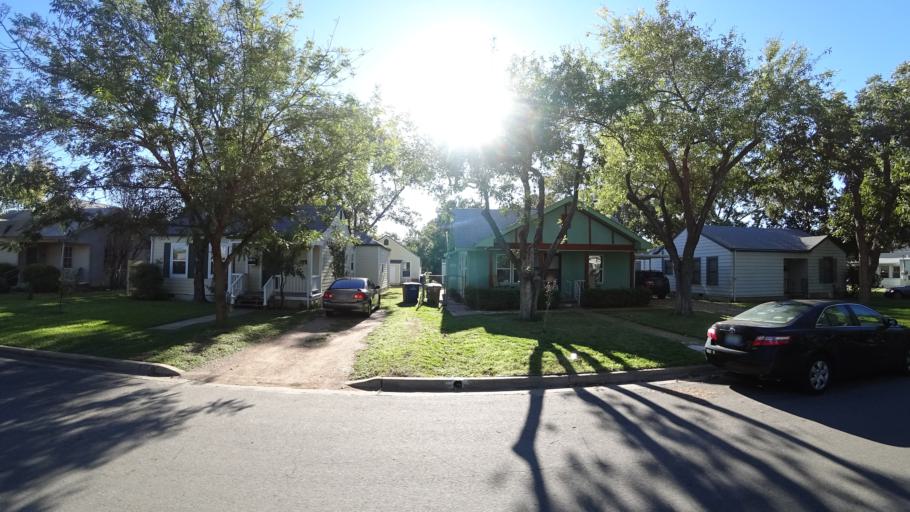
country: US
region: Texas
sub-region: Travis County
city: Austin
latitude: 30.3169
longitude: -97.7206
